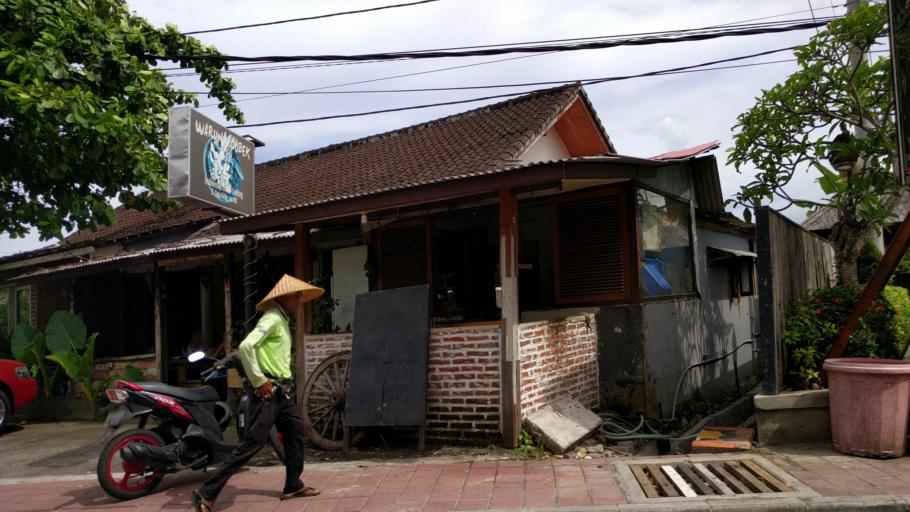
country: ID
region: Bali
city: Kuta
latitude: -8.6722
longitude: 115.1564
